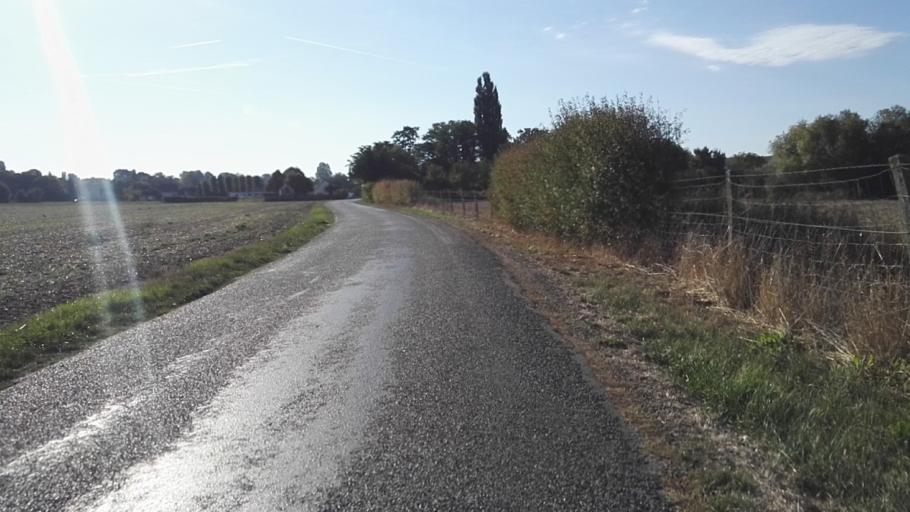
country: FR
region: Haute-Normandie
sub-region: Departement de l'Eure
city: Menilles
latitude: 49.0465
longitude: 1.3369
